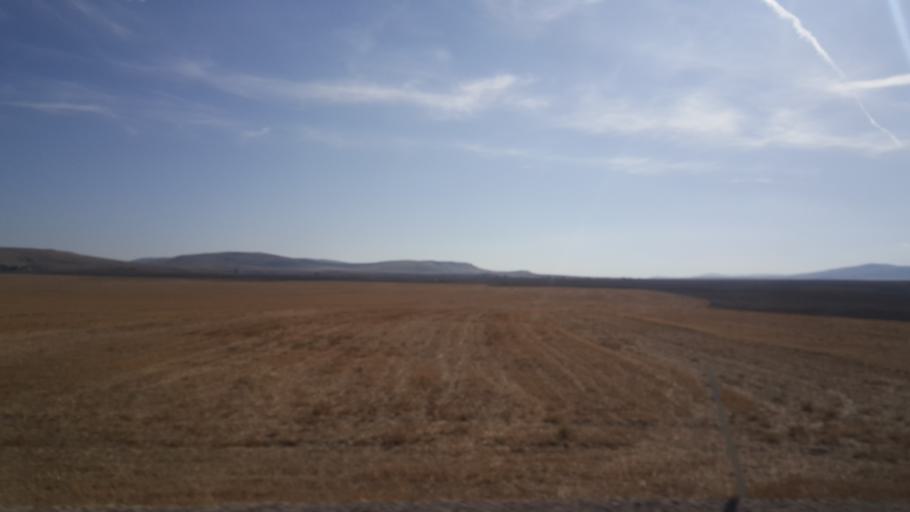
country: TR
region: Ankara
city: Yenice
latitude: 39.3816
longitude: 32.7933
